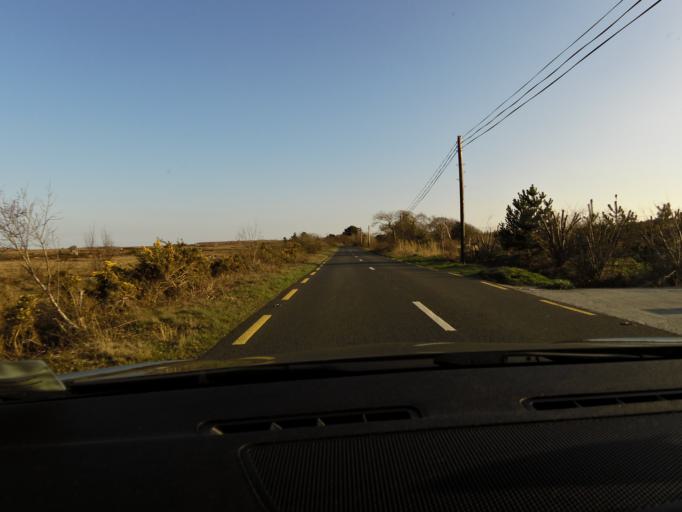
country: IE
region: Connaught
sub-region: County Galway
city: Oughterard
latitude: 53.3738
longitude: -9.5445
